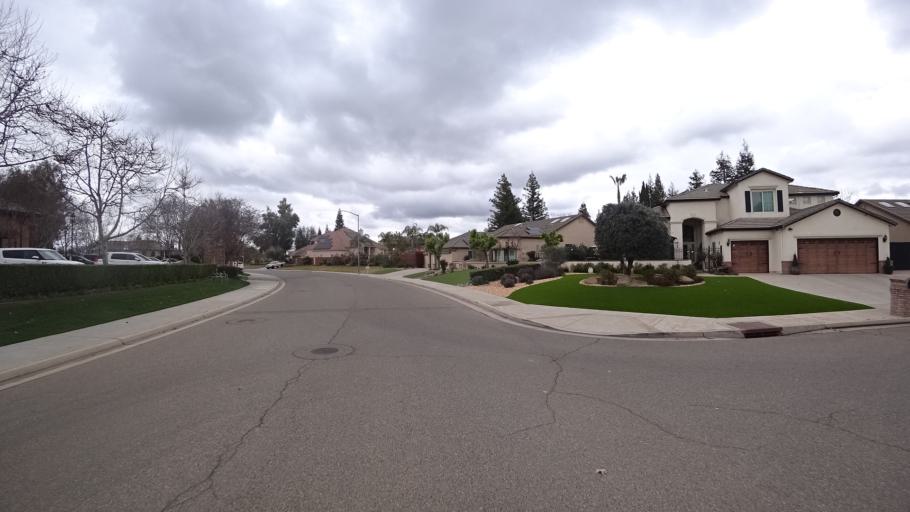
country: US
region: California
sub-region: Fresno County
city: Fresno
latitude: 36.8381
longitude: -119.8343
